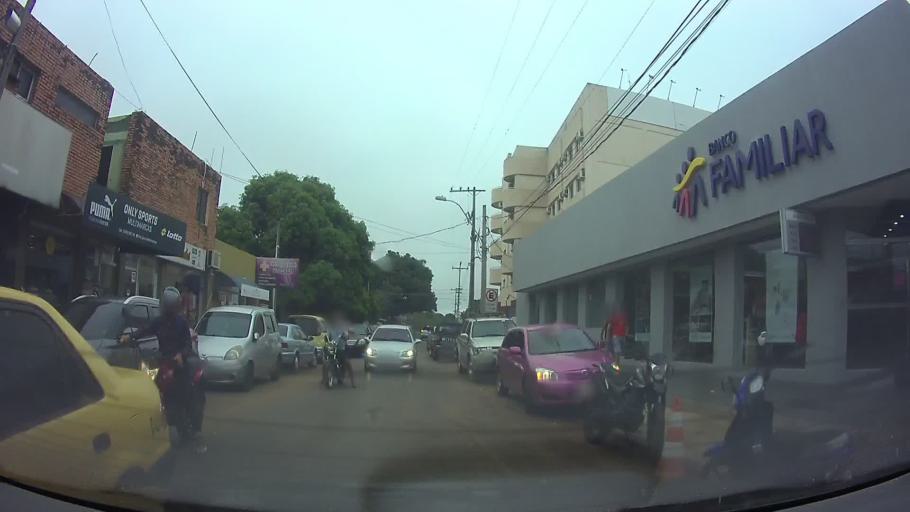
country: PY
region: Central
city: Itaugua
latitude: -25.3927
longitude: -57.3538
